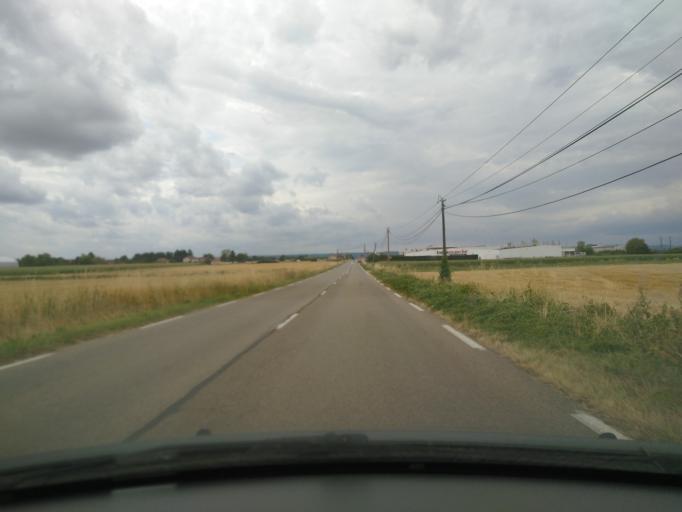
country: FR
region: Rhone-Alpes
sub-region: Departement de l'Isere
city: Beaurepaire
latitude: 45.3754
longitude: 5.0261
